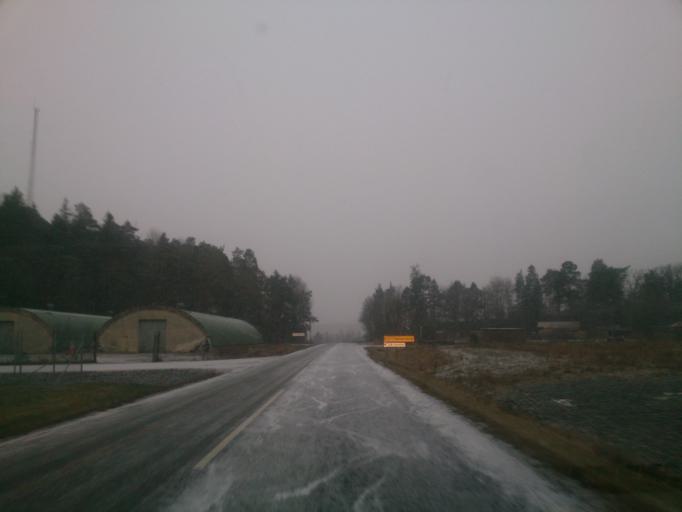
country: SE
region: OEstergoetland
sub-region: Soderkopings Kommun
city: Soederkoeping
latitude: 58.4969
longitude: 16.3102
